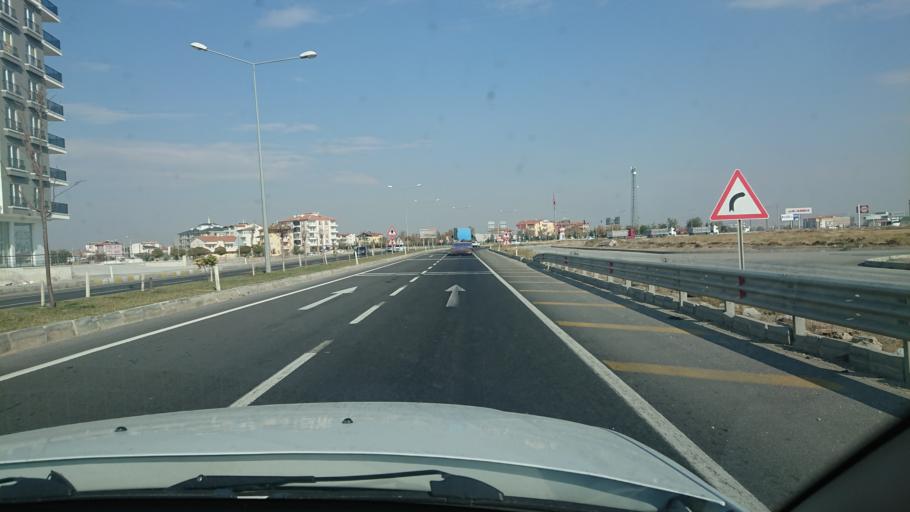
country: TR
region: Aksaray
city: Aksaray
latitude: 38.3545
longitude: 33.9683
